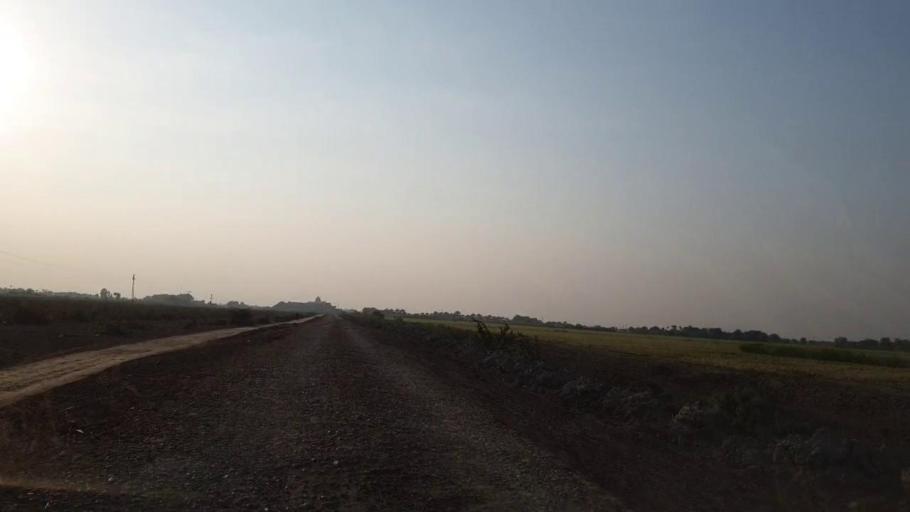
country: PK
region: Sindh
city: Pithoro
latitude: 25.6527
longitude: 69.2401
